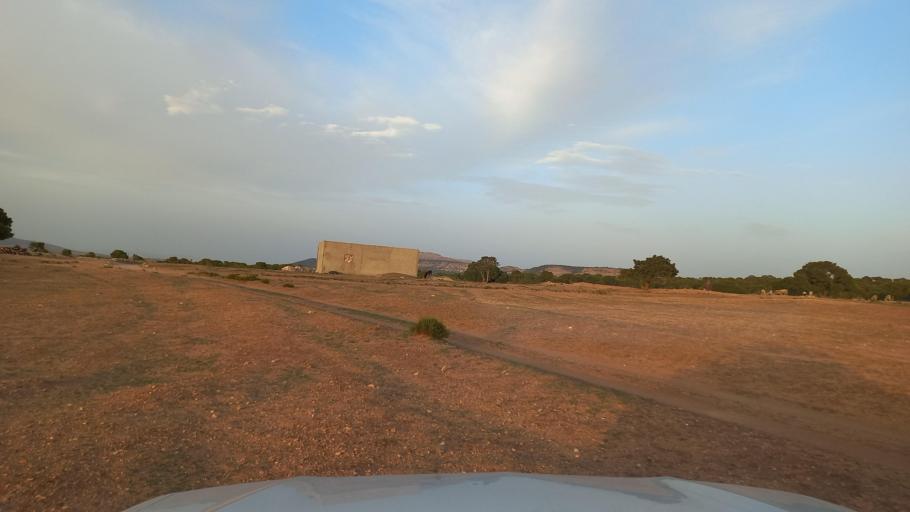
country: TN
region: Al Qasrayn
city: Sbiba
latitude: 35.4215
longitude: 8.9095
